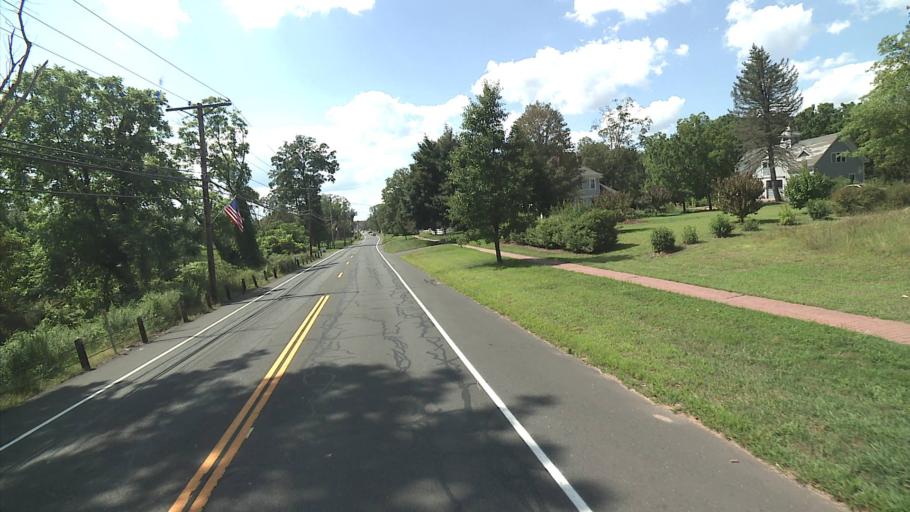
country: US
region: Connecticut
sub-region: Tolland County
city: Somers
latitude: 41.9850
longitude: -72.4373
